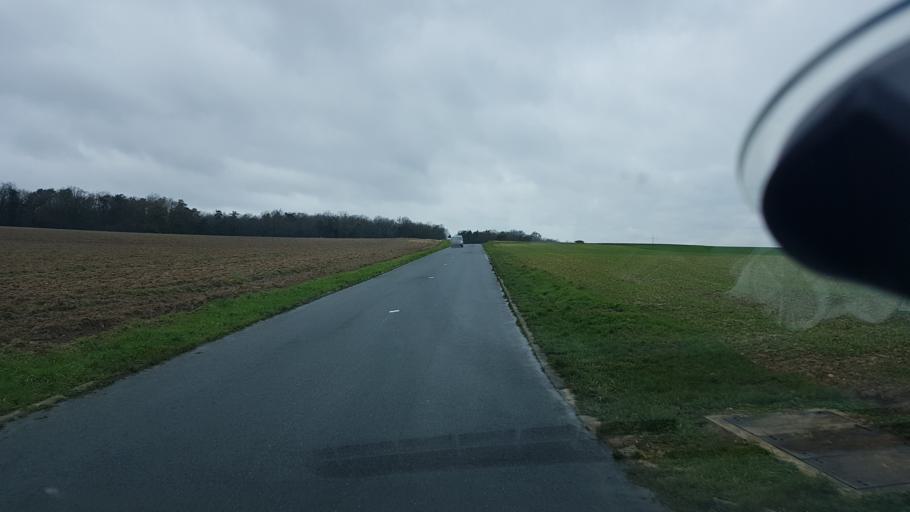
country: FR
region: Ile-de-France
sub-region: Departement de Seine-et-Marne
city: Montigny-sur-Loing
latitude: 48.2753
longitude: 2.7910
